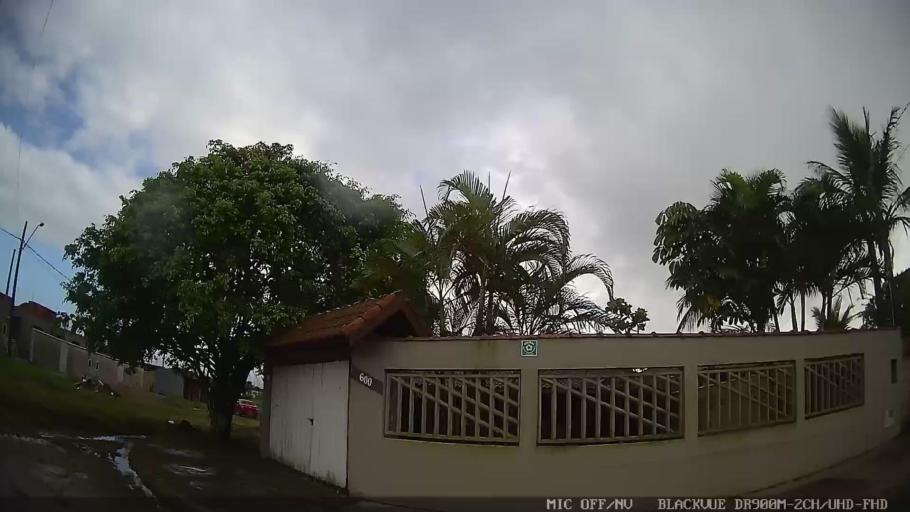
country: BR
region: Sao Paulo
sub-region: Itanhaem
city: Itanhaem
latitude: -24.2028
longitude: -46.8377
